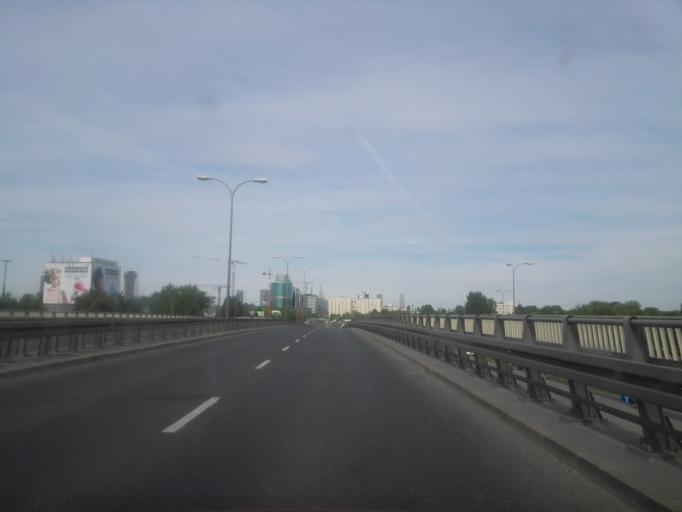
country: PL
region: Masovian Voivodeship
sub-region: Warszawa
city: Ochota
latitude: 52.2162
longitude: 20.9610
